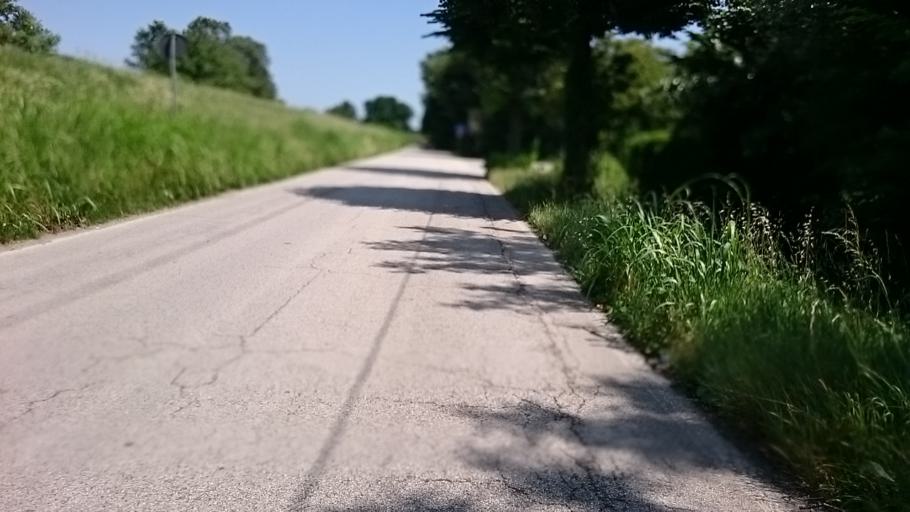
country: IT
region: Veneto
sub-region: Provincia di Padova
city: San Vito
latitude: 45.4239
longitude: 11.9563
